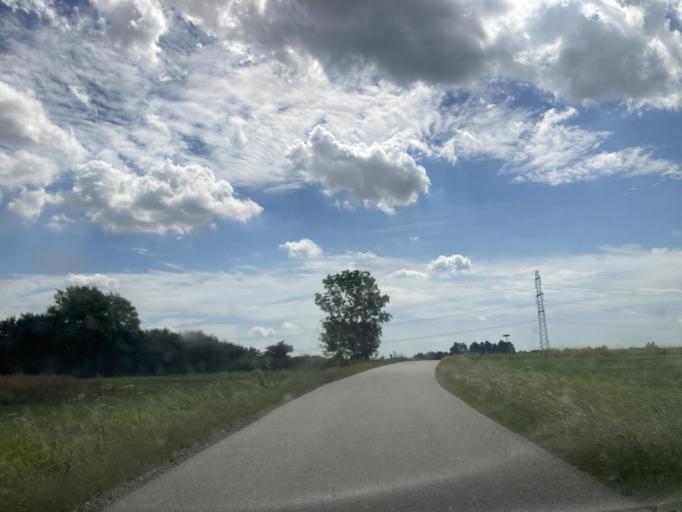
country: DK
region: Zealand
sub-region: Koge Kommune
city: Borup
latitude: 55.4555
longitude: 11.9487
